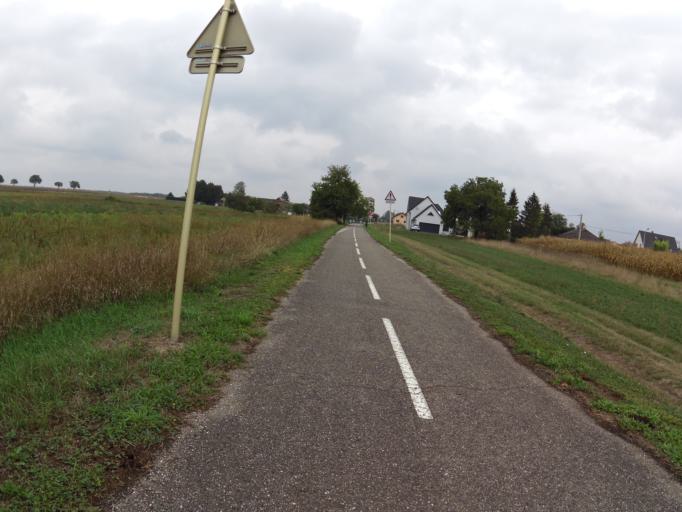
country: FR
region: Alsace
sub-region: Departement du Haut-Rhin
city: Fessenheim
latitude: 47.9270
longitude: 7.5344
